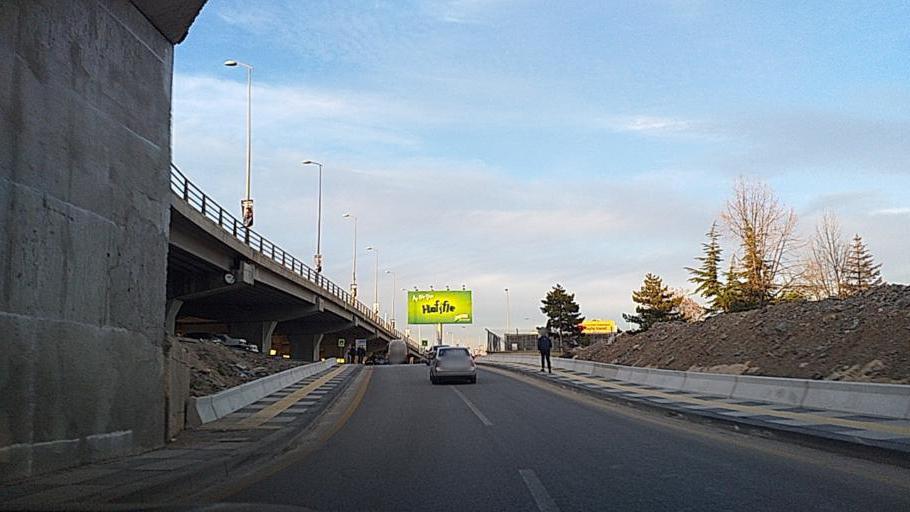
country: TR
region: Ankara
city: Ankara
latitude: 39.9501
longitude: 32.8350
